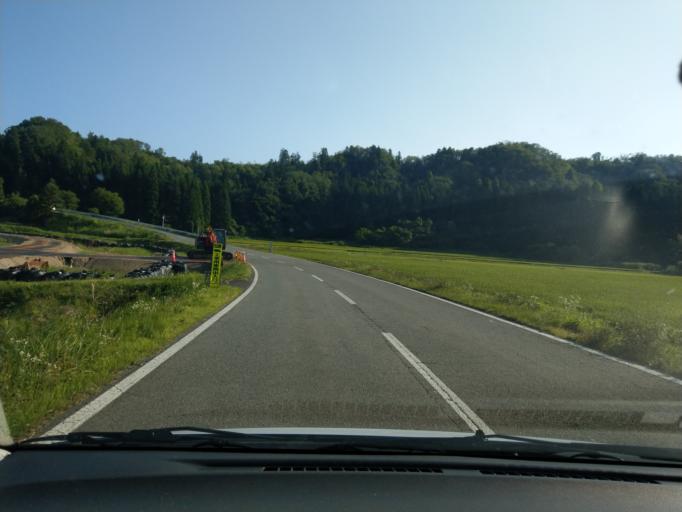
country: JP
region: Akita
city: Akita
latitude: 39.5941
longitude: 140.2329
